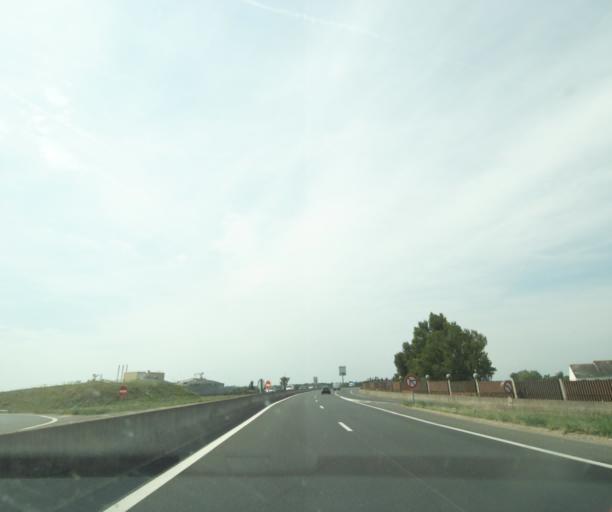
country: FR
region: Centre
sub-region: Departement d'Indre-et-Loire
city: La Riche
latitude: 47.3768
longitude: 0.6508
